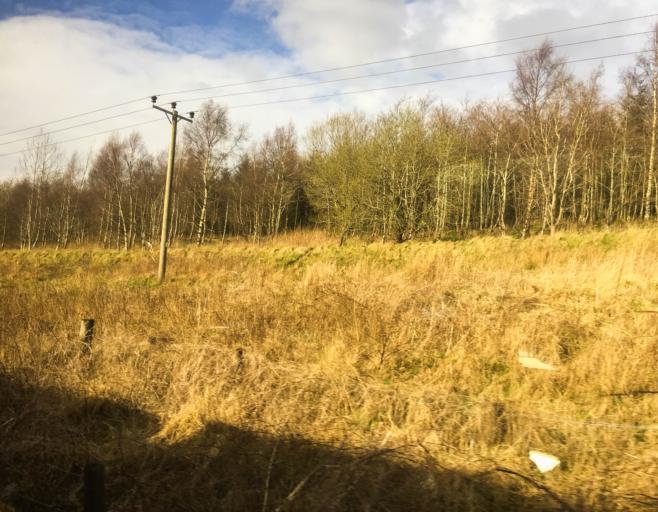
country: GB
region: Scotland
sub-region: North Lanarkshire
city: Glenboig
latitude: 55.8812
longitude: -4.0543
